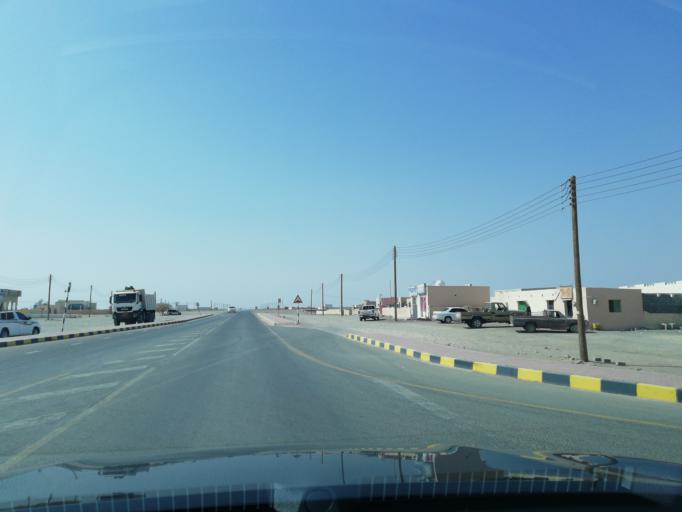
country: OM
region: Muhafazat ad Dakhiliyah
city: Adam
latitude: 22.2988
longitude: 58.0750
